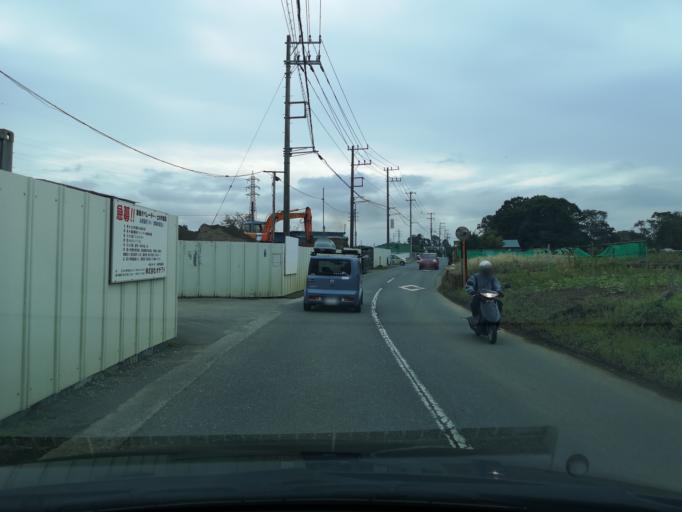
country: JP
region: Kanagawa
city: Atsugi
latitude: 35.3893
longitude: 139.3912
